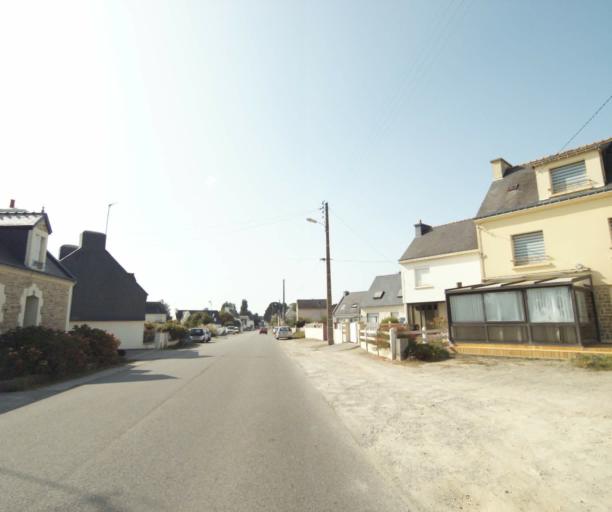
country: FR
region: Brittany
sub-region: Departement du Morbihan
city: Riantec
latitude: 47.7126
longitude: -3.3036
